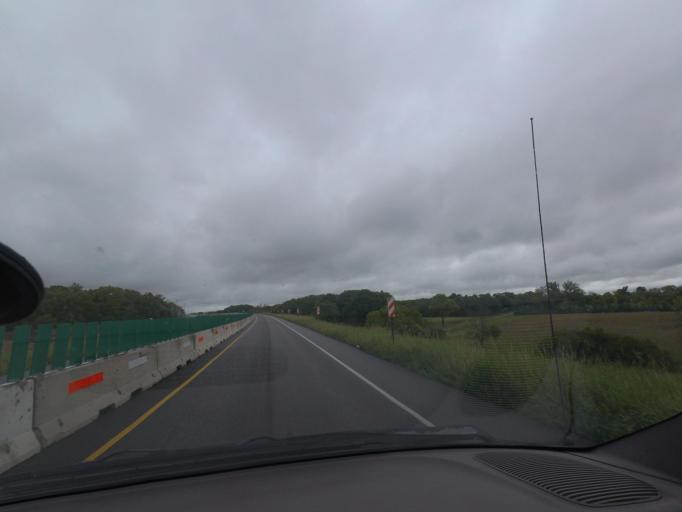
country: US
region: Illinois
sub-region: Piatt County
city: Cerro Gordo
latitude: 39.9819
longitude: -88.7911
